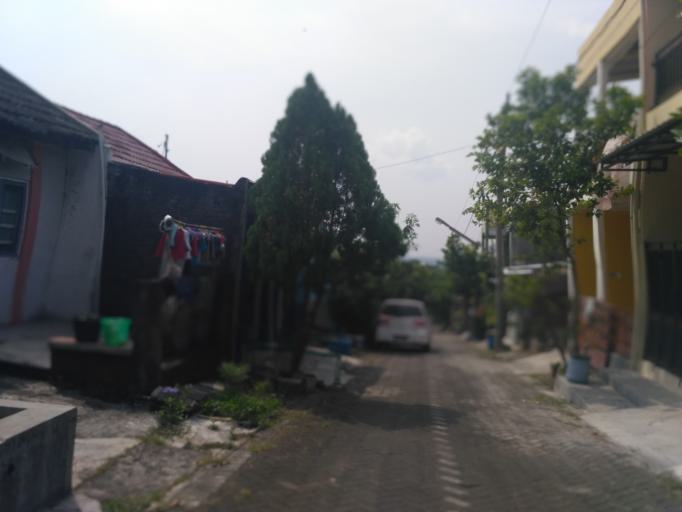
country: ID
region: Central Java
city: Mranggen
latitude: -7.0641
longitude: 110.4574
